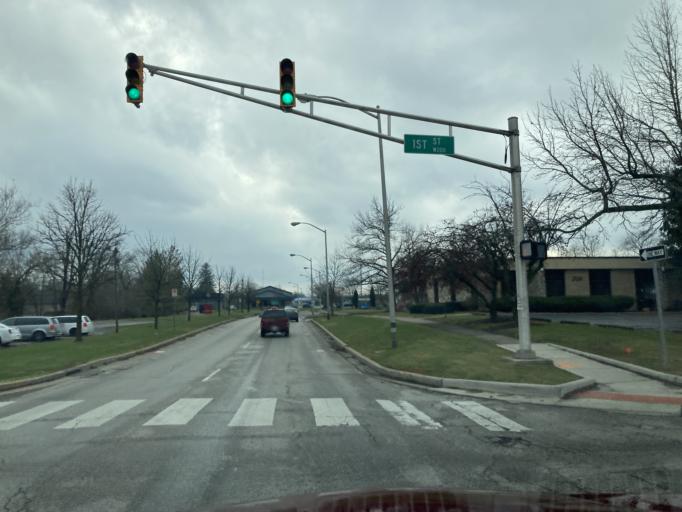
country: US
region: Indiana
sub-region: Monroe County
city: Bloomington
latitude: 39.1595
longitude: -86.5350
